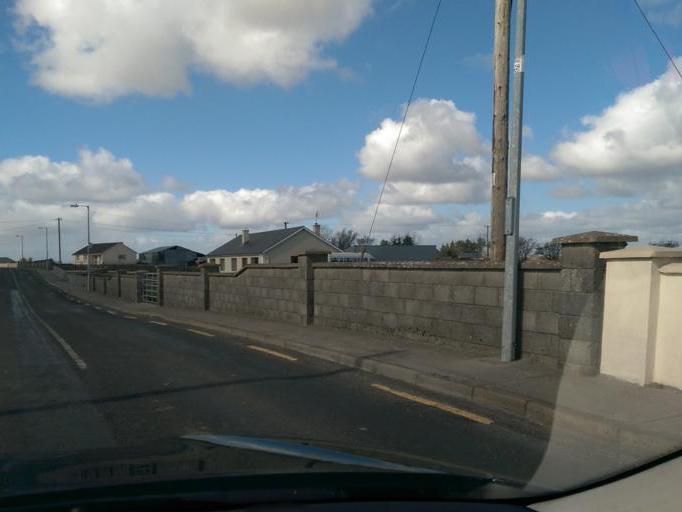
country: IE
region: Connaught
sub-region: County Galway
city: Athenry
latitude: 53.4234
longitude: -8.5852
